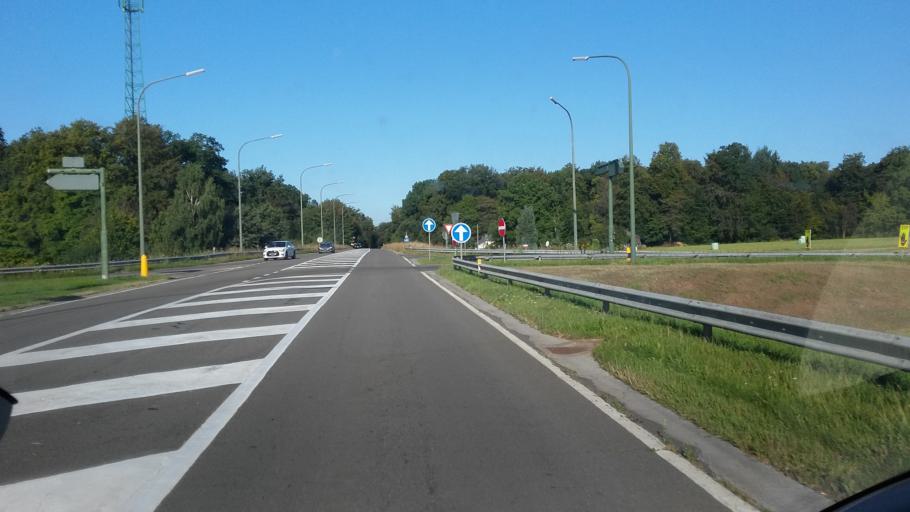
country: BE
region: Wallonia
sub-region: Province du Luxembourg
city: Leglise
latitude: 49.8083
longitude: 5.5169
